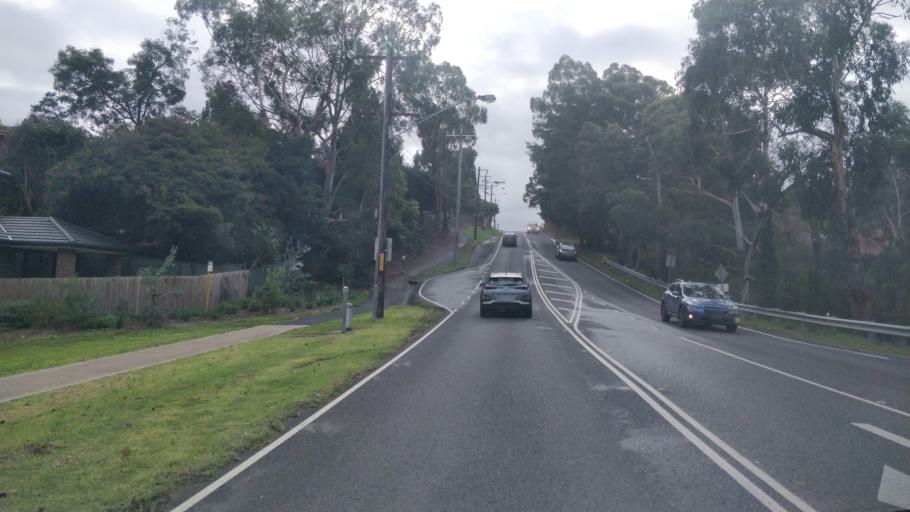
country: AU
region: Victoria
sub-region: Manningham
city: Donvale
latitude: -37.7757
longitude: 145.1829
